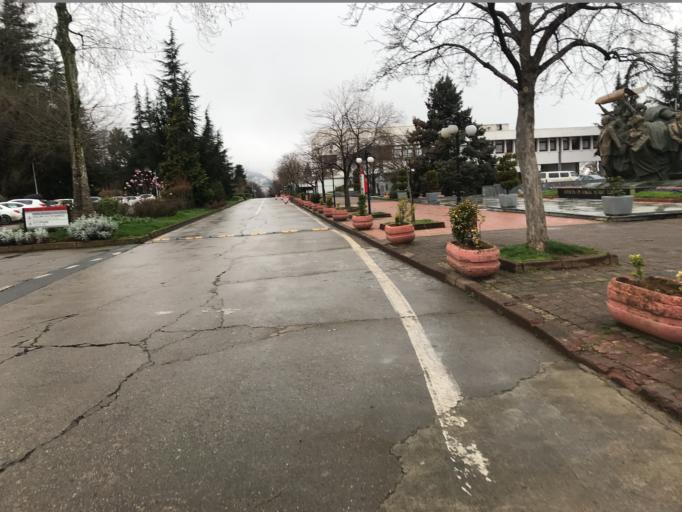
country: TR
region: Trabzon
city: Trabzon
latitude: 40.9975
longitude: 39.7719
